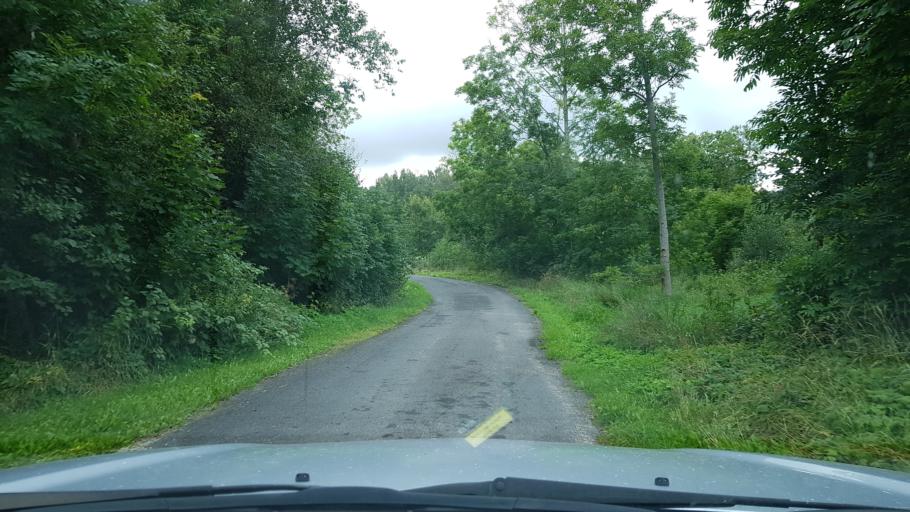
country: EE
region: Harju
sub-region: Rae vald
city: Jueri
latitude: 59.3591
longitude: 24.9376
